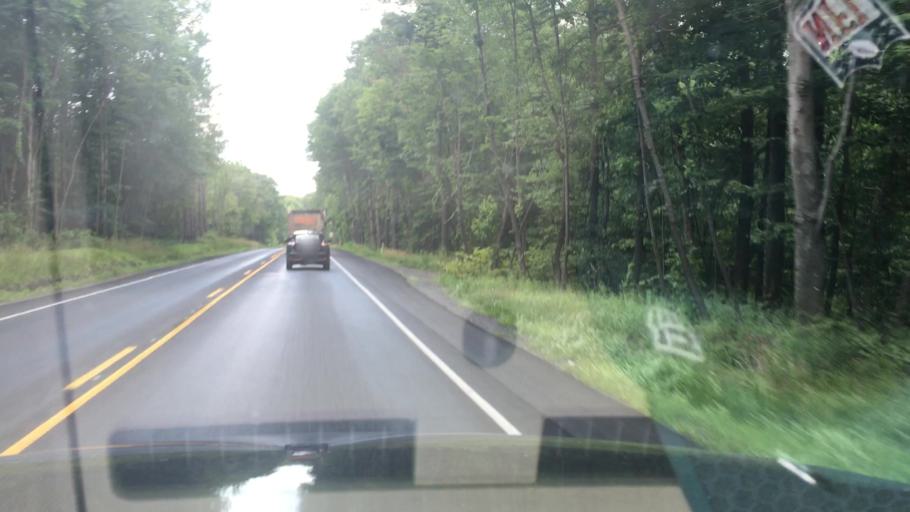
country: US
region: Pennsylvania
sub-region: Northumberland County
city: Mount Carmel
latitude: 40.7673
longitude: -76.4222
